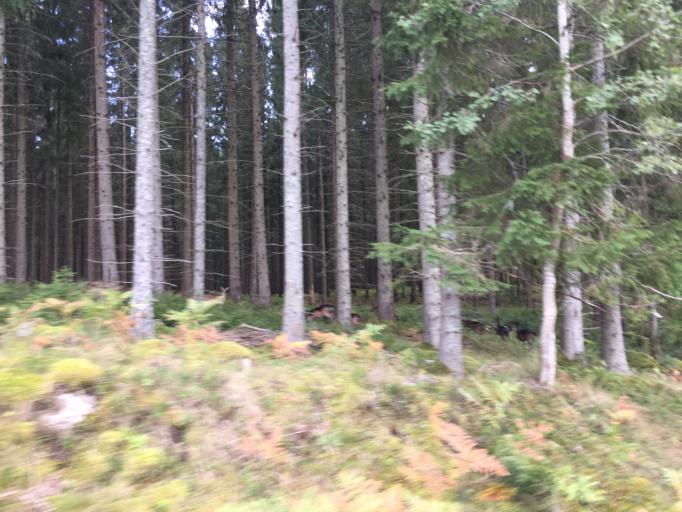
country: SE
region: Soedermanland
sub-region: Vingakers Kommun
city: Vingaker
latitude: 58.9583
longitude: 15.6839
